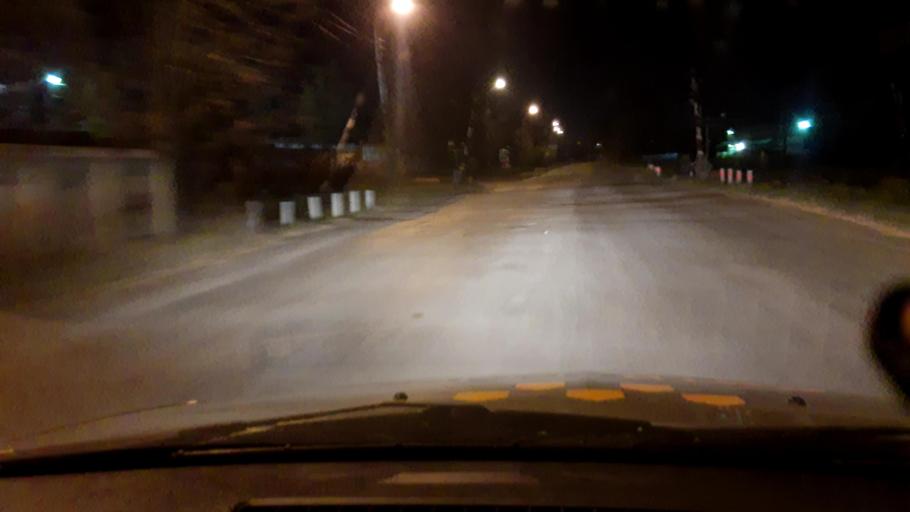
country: RU
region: Bashkortostan
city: Ufa
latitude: 54.8370
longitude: 56.0826
